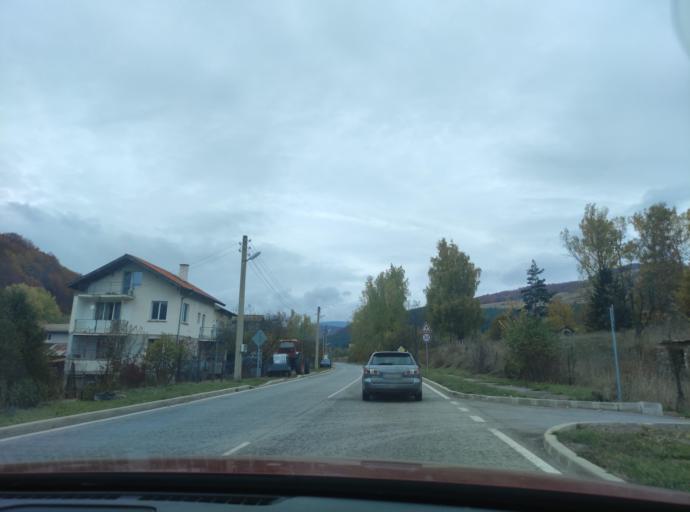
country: BG
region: Sofiya
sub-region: Obshtina Godech
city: Godech
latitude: 43.0782
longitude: 23.1073
